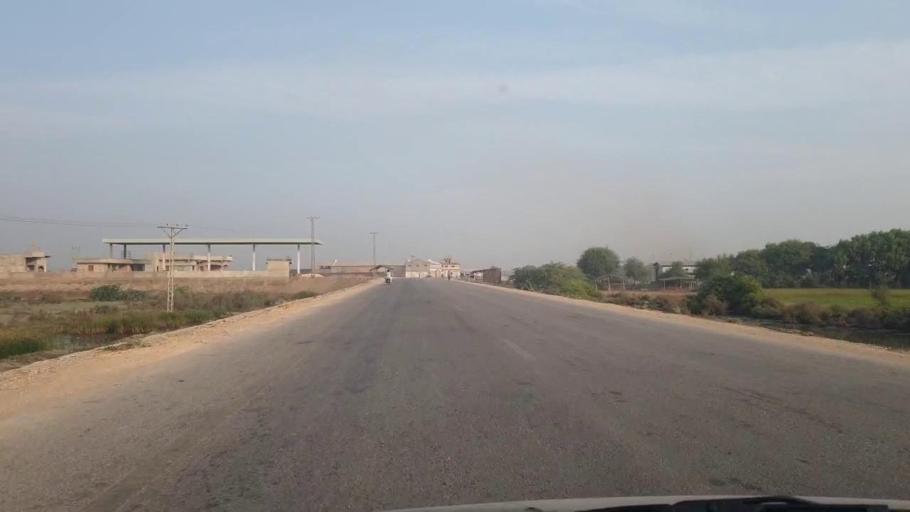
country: PK
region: Sindh
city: Badin
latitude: 24.6835
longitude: 68.8247
